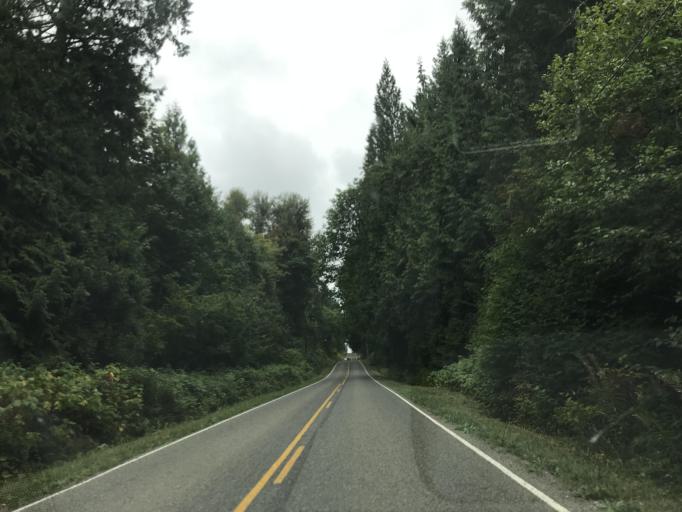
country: US
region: Washington
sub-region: Whatcom County
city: Sudden Valley
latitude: 48.7874
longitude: -122.3331
